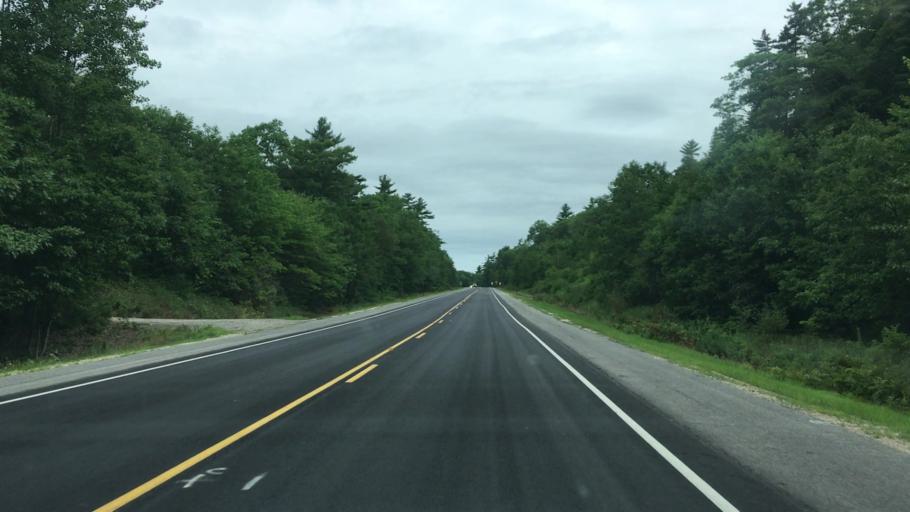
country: US
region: Maine
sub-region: Washington County
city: Cherryfield
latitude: 44.9003
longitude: -67.8558
